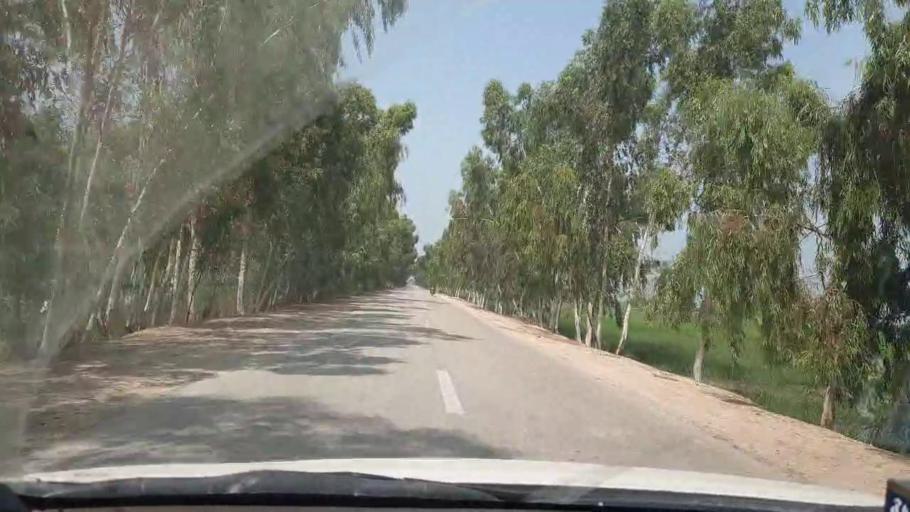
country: PK
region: Sindh
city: Rustam jo Goth
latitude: 27.9577
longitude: 68.7452
